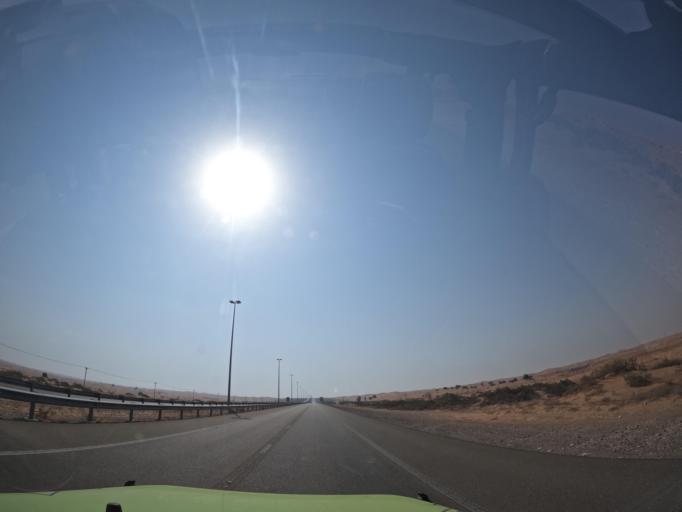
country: OM
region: Al Buraimi
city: Al Buraymi
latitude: 24.4570
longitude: 55.6448
